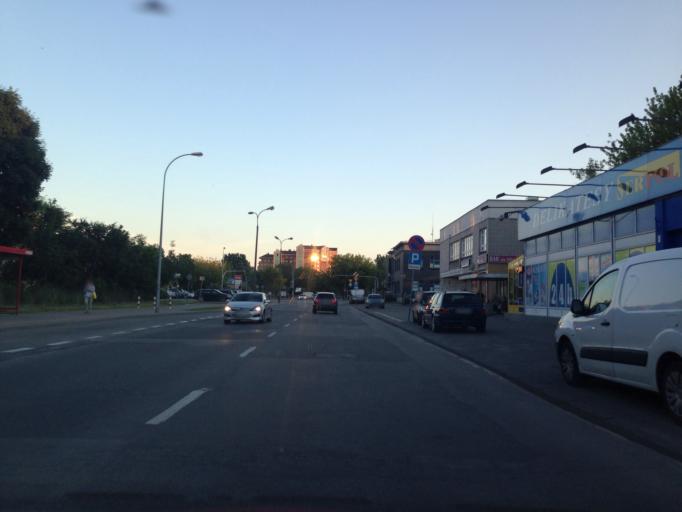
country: PL
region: Masovian Voivodeship
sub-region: Warszawa
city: Bielany
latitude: 52.2716
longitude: 20.9507
